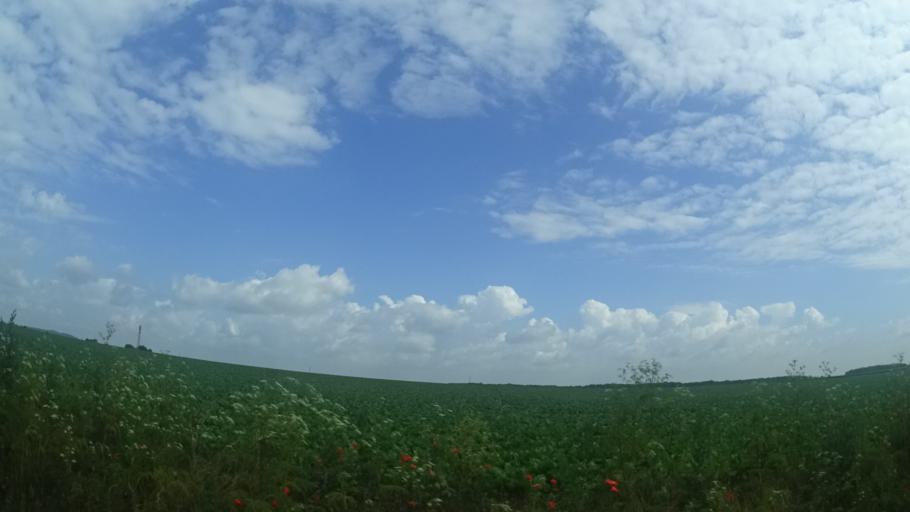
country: DE
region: Lower Saxony
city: Pattensen
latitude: 52.2101
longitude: 9.7215
